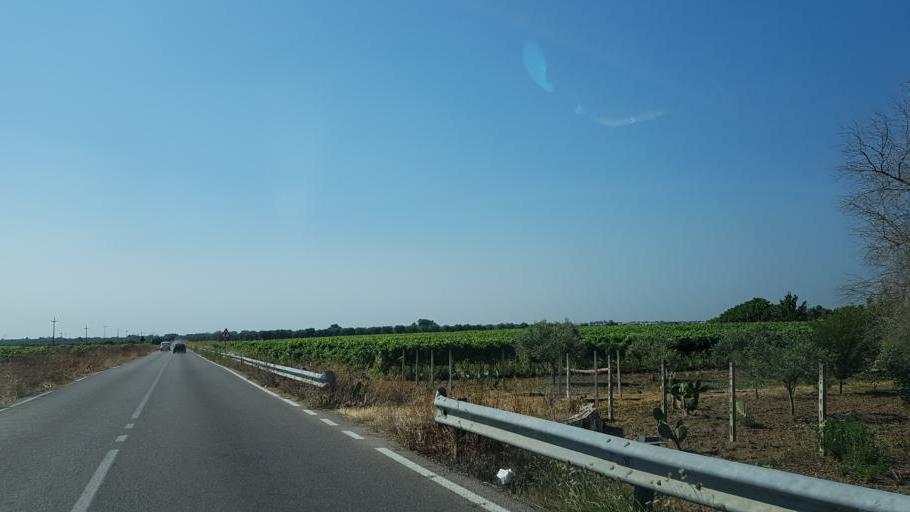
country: IT
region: Apulia
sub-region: Provincia di Brindisi
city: San Donaci
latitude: 40.4293
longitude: 17.9420
